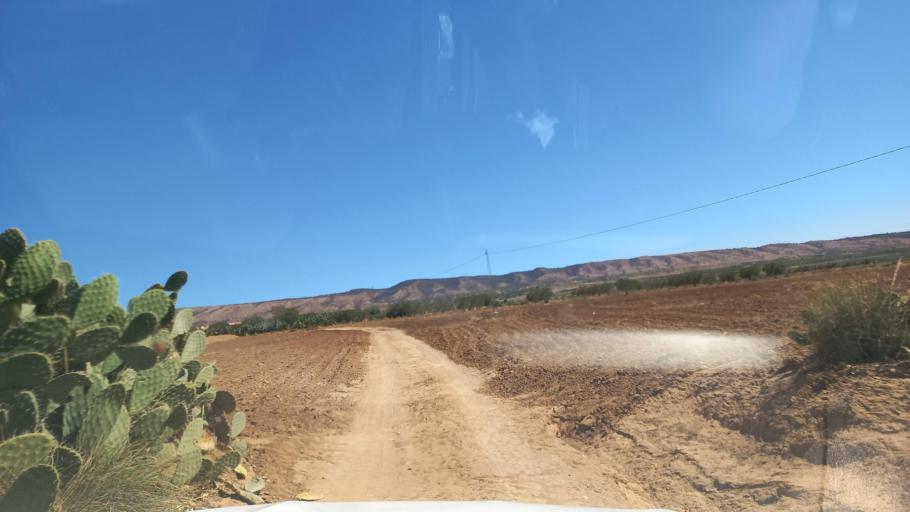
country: TN
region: Al Qasrayn
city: Sbiba
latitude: 35.3505
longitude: 9.1049
